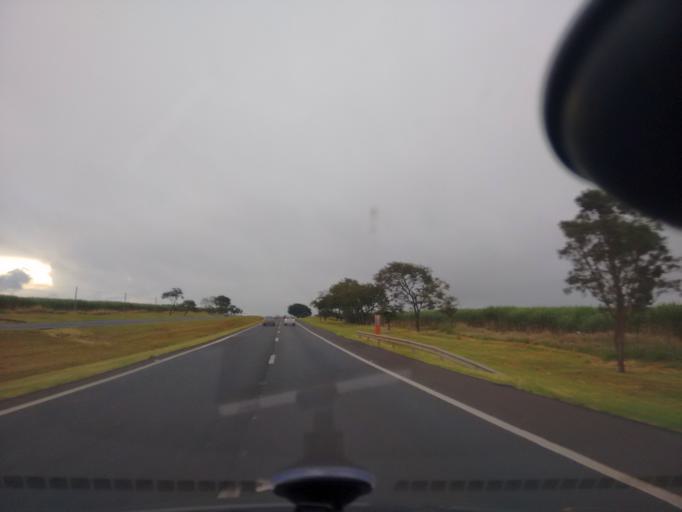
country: BR
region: Sao Paulo
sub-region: Ibate
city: Ibate
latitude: -21.9675
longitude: -47.9602
